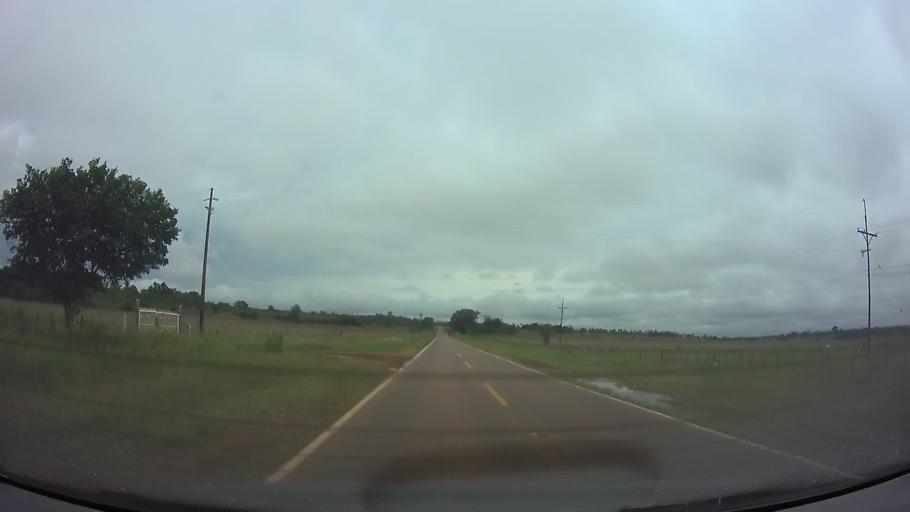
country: PY
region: Paraguari
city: Acahay
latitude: -25.8810
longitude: -57.1225
